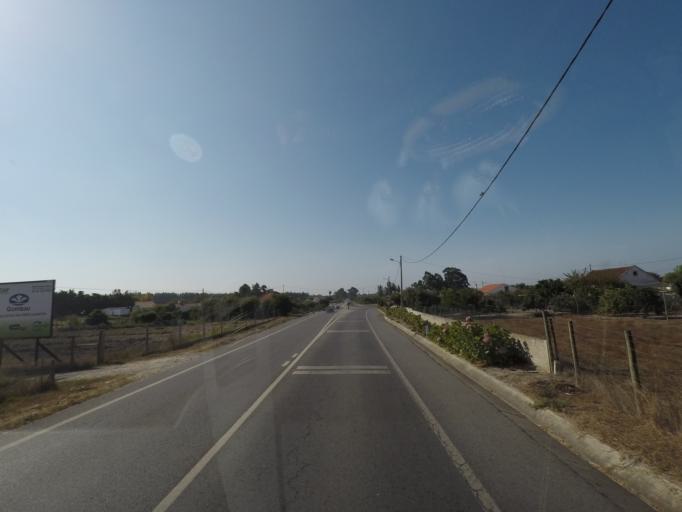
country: PT
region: Beja
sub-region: Odemira
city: Vila Nova de Milfontes
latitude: 37.6576
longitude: -8.7547
